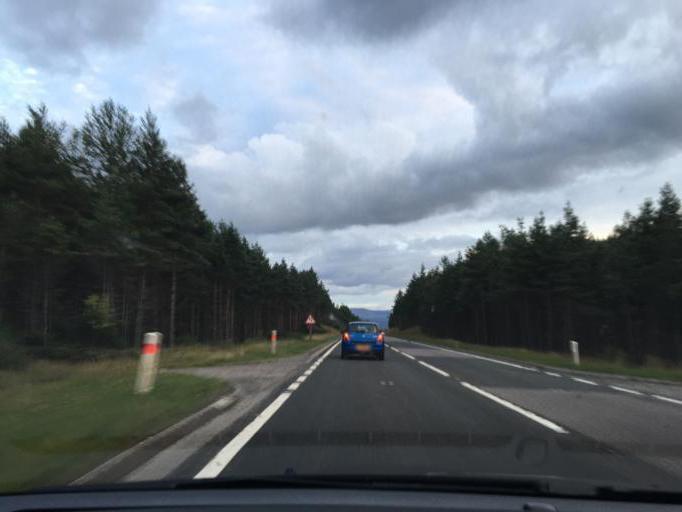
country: GB
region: Scotland
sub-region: Highland
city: Aviemore
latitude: 57.2587
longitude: -3.8097
